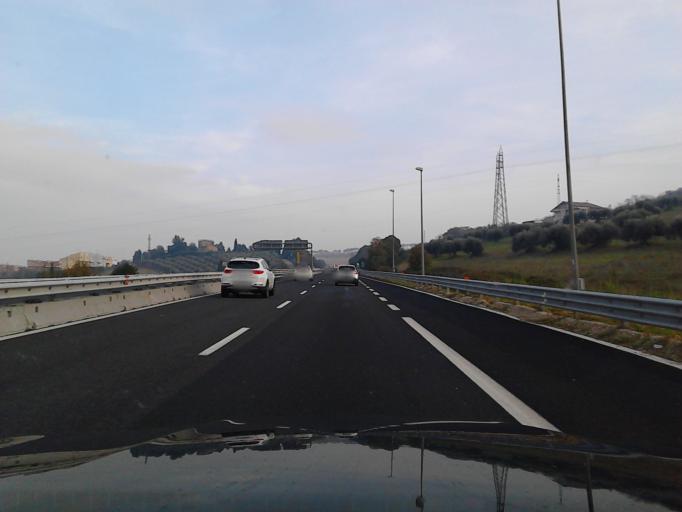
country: IT
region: Abruzzo
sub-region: Provincia di Teramo
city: Borgo Santa Maria Immacolata
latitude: 42.6059
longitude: 14.0499
